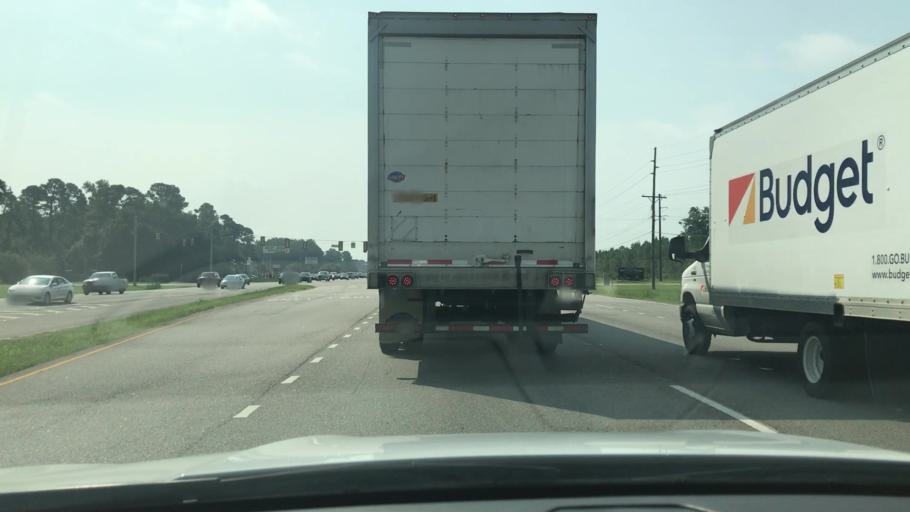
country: US
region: South Carolina
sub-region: Horry County
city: Red Hill
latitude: 33.7833
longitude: -78.9904
